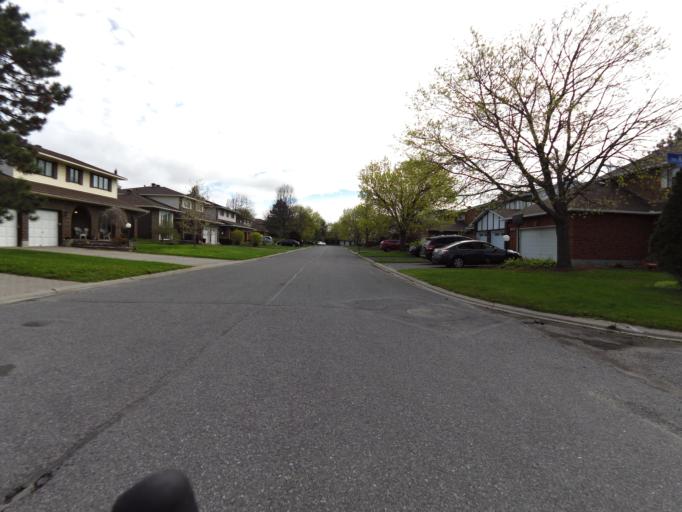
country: CA
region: Ontario
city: Bells Corners
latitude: 45.2919
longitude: -75.7464
